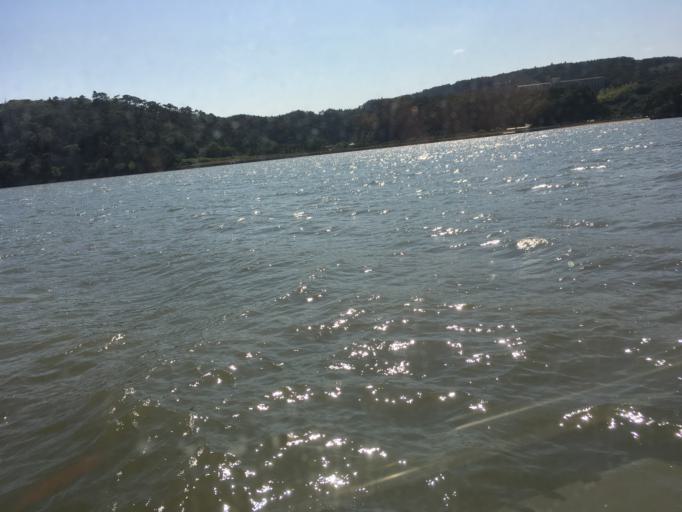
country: JP
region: Miyagi
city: Matsushima
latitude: 38.3632
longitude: 141.0675
